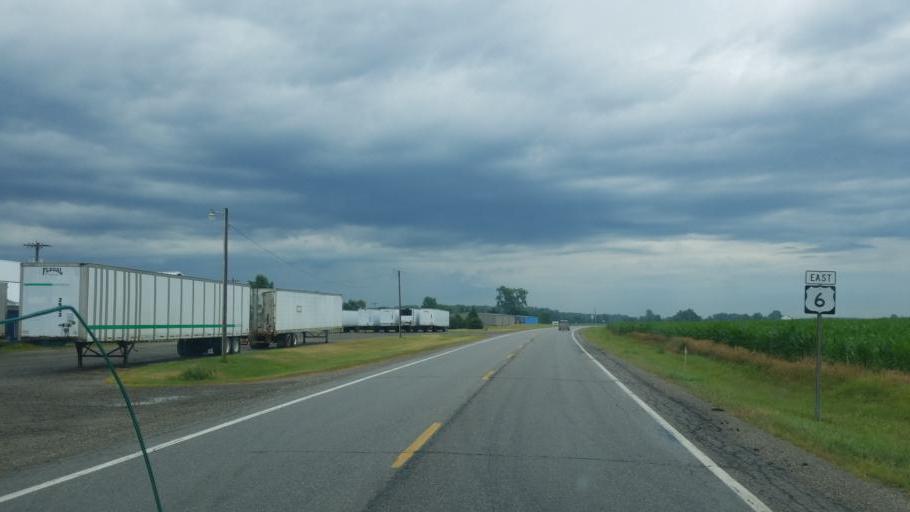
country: US
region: Ohio
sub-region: Williams County
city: Edgerton
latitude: 41.4482
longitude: -84.6910
